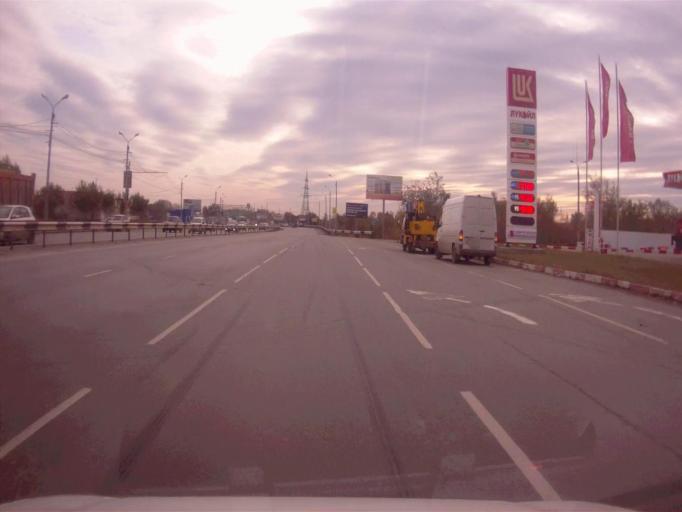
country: RU
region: Chelyabinsk
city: Novosineglazovskiy
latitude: 55.0758
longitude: 61.3883
